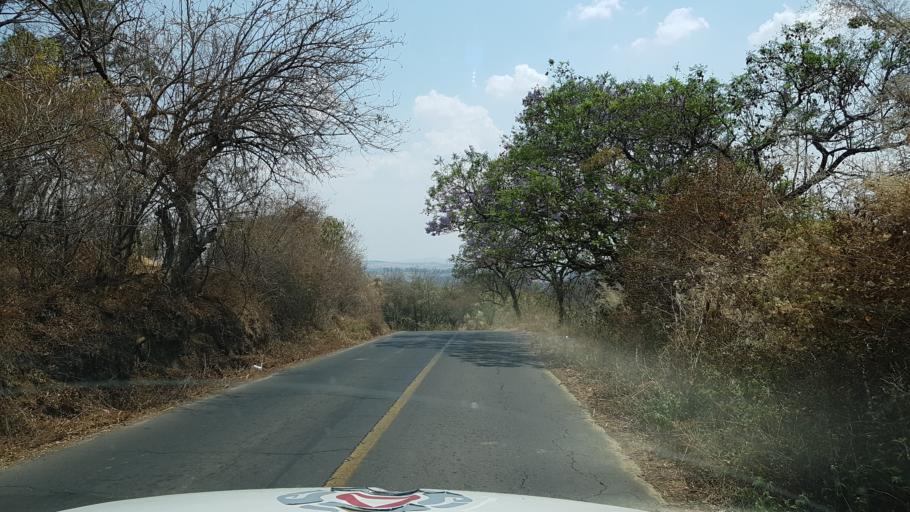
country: MX
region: Morelos
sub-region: Yecapixtla
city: Texcala
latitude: 18.9010
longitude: -98.8096
